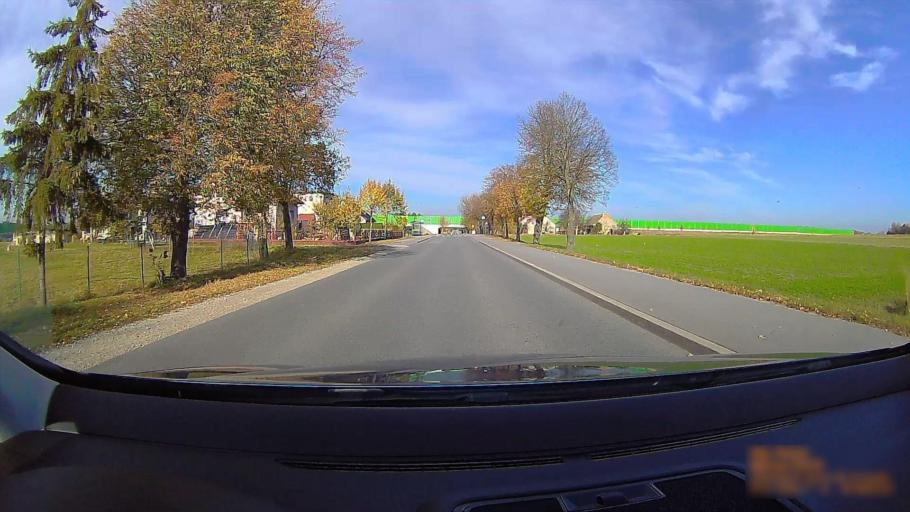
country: PL
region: Greater Poland Voivodeship
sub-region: Powiat kepinski
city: Kepno
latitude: 51.3128
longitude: 18.0142
